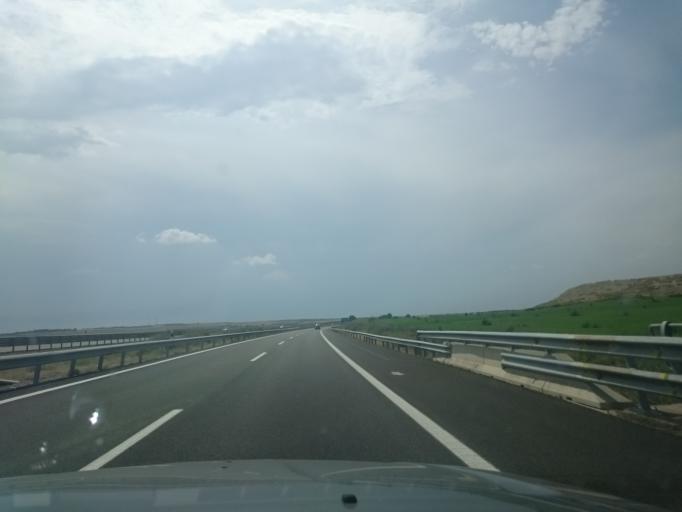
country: ES
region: Aragon
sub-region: Provincia de Zaragoza
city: Bujaraloz
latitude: 41.5167
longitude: -0.1310
